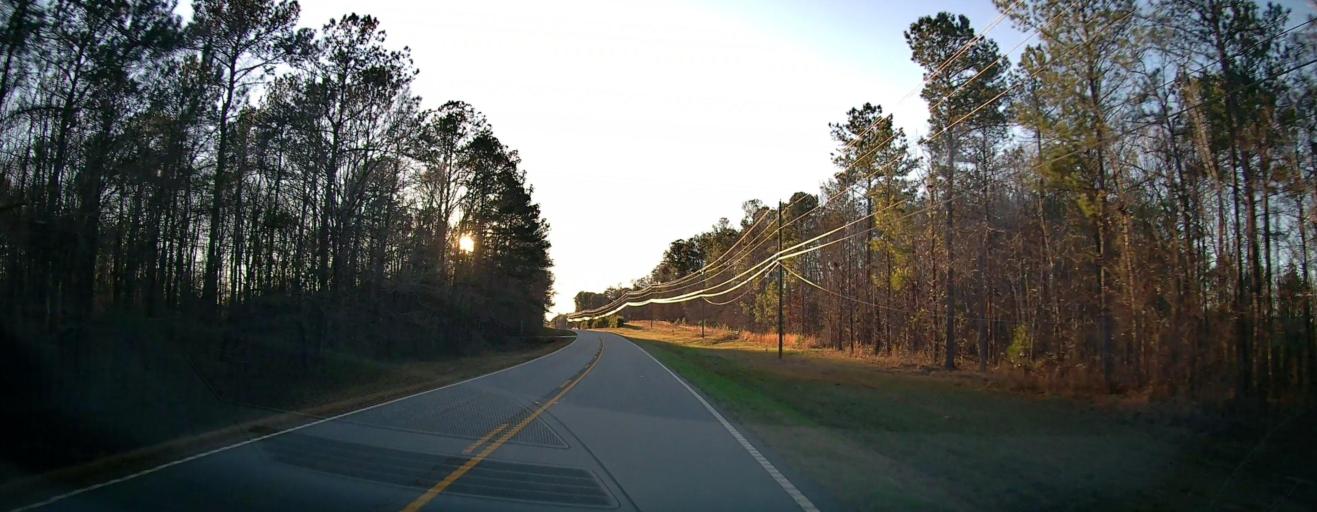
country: US
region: Georgia
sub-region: Harris County
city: Hamilton
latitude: 32.6728
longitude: -84.9250
